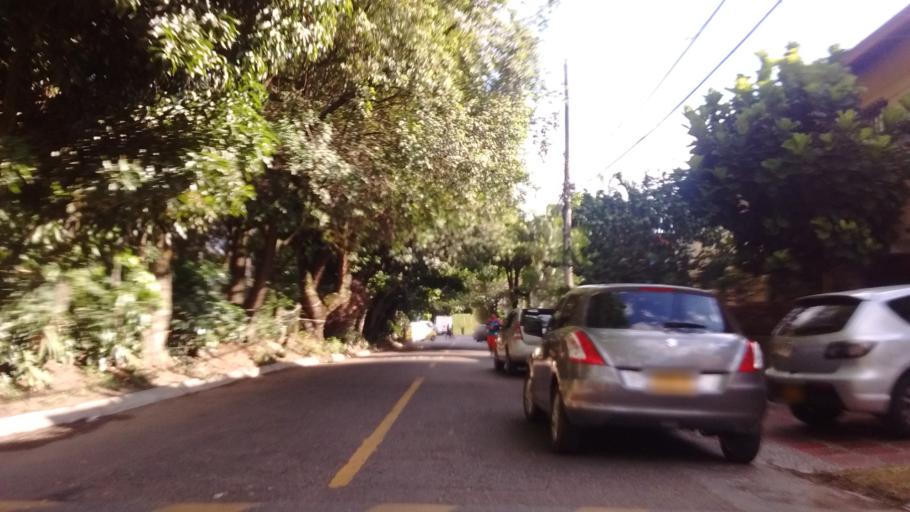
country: CO
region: Antioquia
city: Medellin
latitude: 6.2577
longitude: -75.6115
